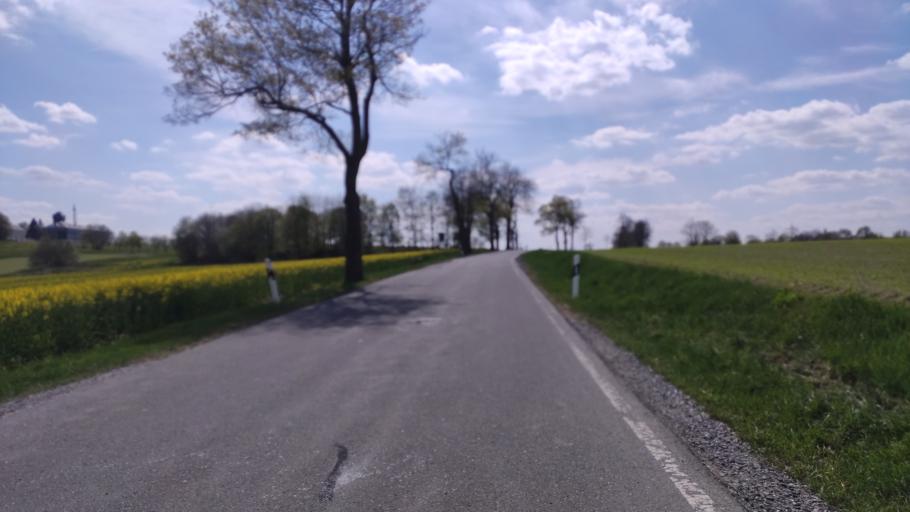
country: DE
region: Bavaria
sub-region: Upper Franconia
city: Ludwigsstadt
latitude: 50.4845
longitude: 11.4504
